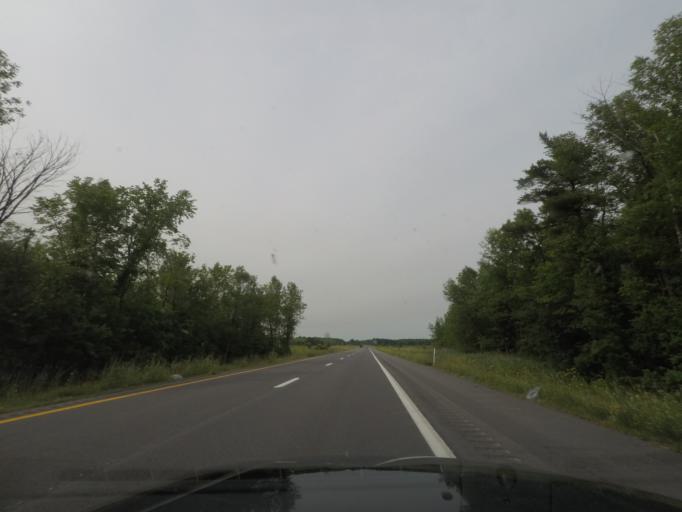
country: US
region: New York
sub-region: Clinton County
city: Cumberland Head
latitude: 44.8299
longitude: -73.4465
